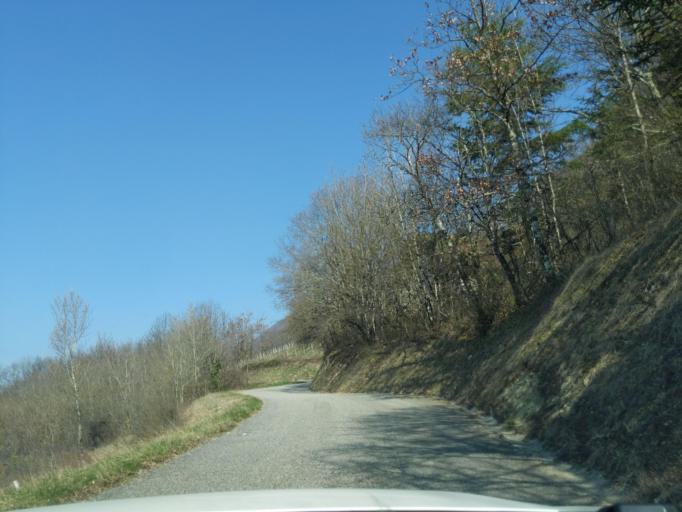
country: FR
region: Rhone-Alpes
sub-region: Departement de la Haute-Savoie
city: Moye
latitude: 45.8903
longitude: 5.8487
